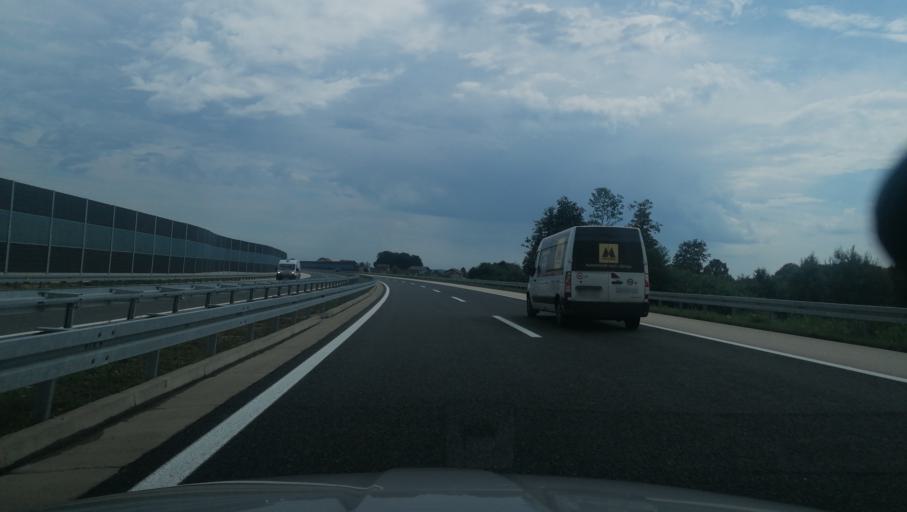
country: BA
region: Republika Srpska
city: Stanari
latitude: 44.8113
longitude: 17.8578
